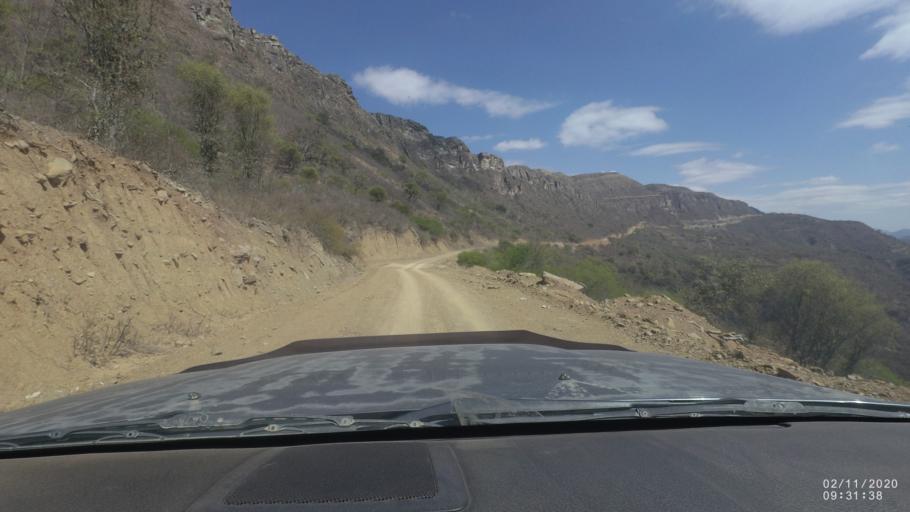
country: BO
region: Chuquisaca
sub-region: Provincia Zudanez
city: Mojocoya
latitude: -18.4267
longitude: -64.5833
